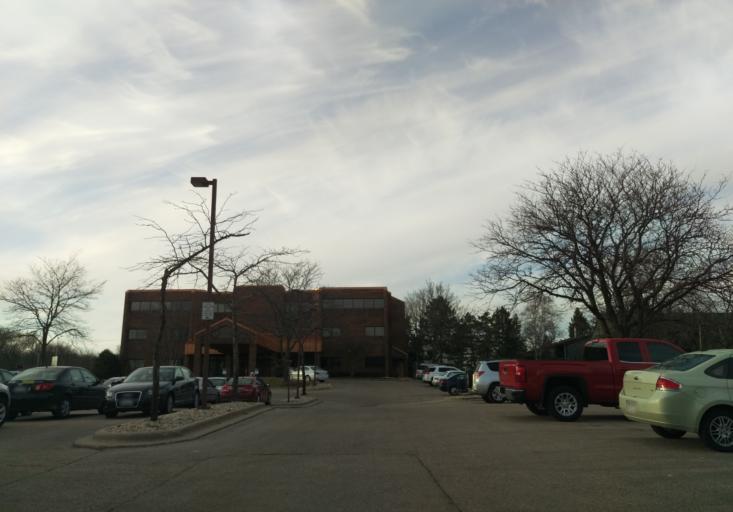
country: US
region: Wisconsin
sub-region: Dane County
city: Middleton
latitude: 43.1038
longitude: -89.4856
